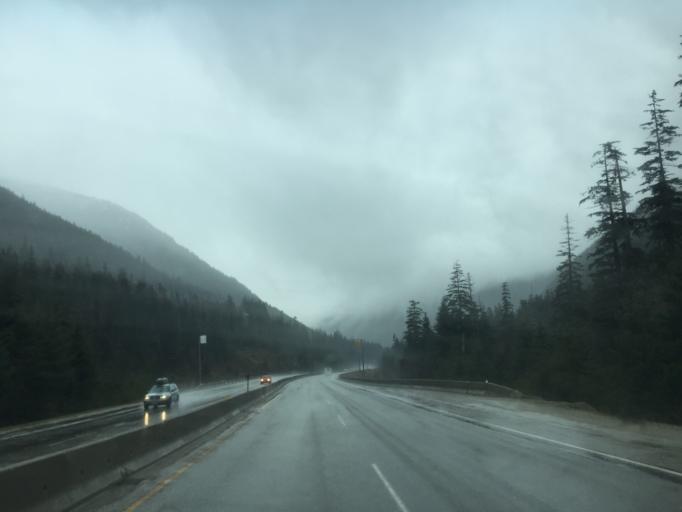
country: CA
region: British Columbia
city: Hope
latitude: 49.5509
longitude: -121.1935
